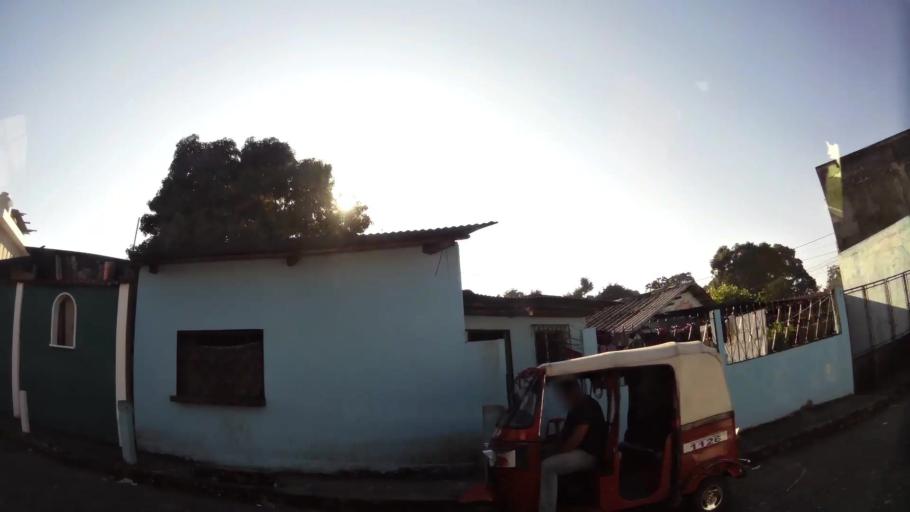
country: GT
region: Suchitepeque
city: Mazatenango
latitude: 14.5325
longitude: -91.5144
